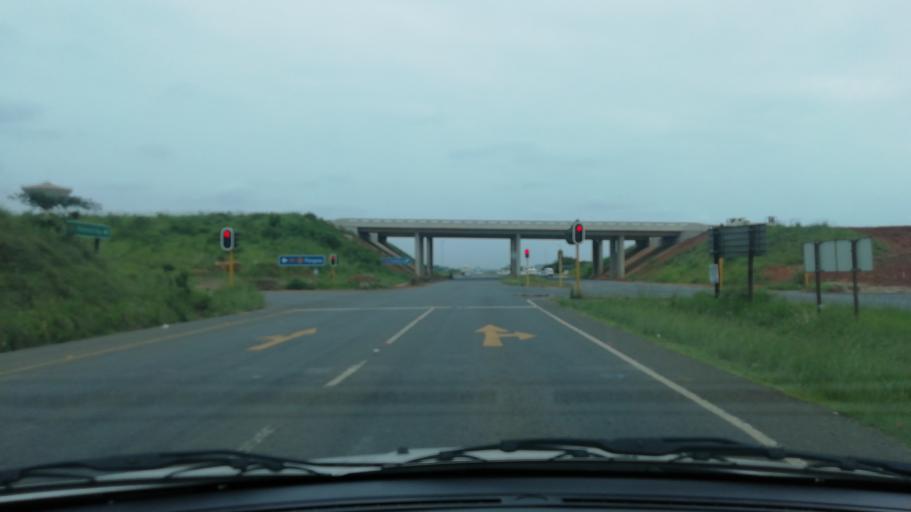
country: ZA
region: KwaZulu-Natal
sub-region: uThungulu District Municipality
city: Empangeni
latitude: -28.7685
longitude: 31.9294
